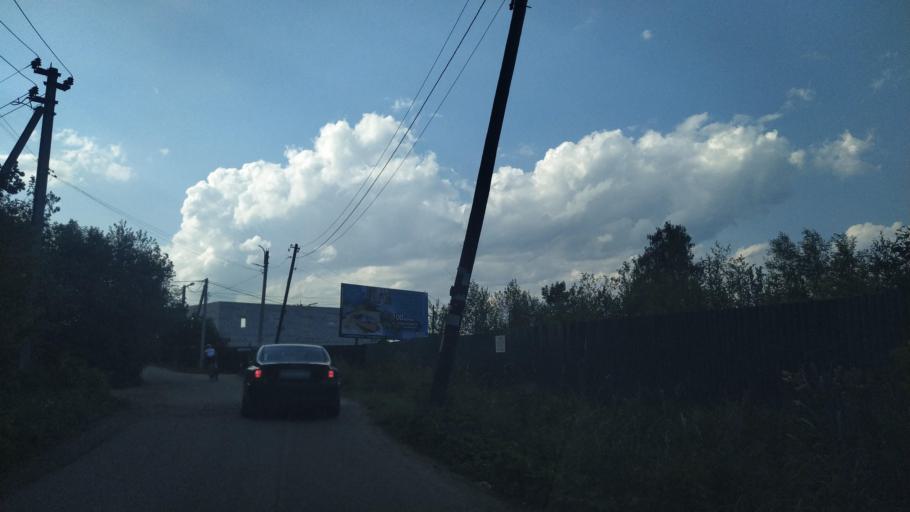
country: RU
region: Leningrad
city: Toksovo
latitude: 60.1735
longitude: 30.5283
